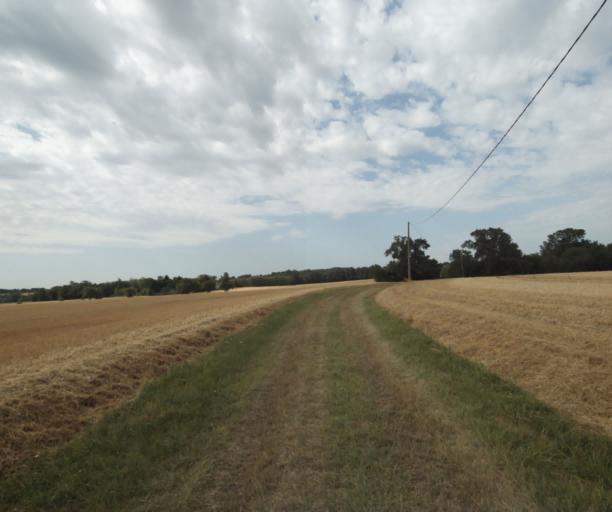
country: FR
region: Midi-Pyrenees
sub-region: Departement de la Haute-Garonne
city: Saint-Felix-Lauragais
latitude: 43.4368
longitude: 1.9261
